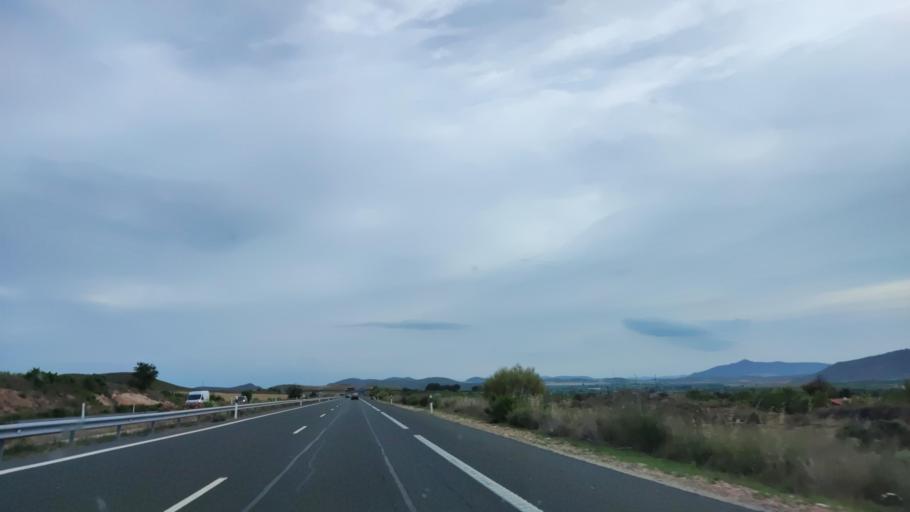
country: ES
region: Castille-La Mancha
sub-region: Provincia de Albacete
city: Tobarra
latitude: 38.6216
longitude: -1.6753
